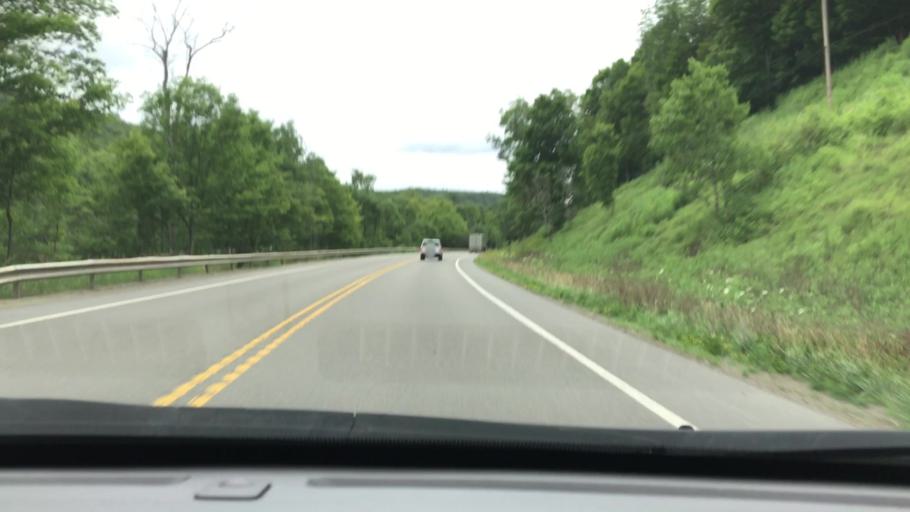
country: US
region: Pennsylvania
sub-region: McKean County
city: Kane
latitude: 41.6756
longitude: -78.6842
